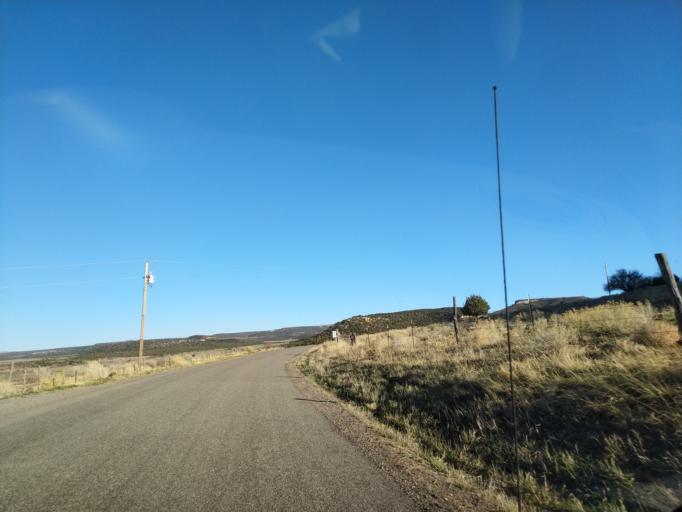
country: US
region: Colorado
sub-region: Mesa County
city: Loma
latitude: 38.9509
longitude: -108.9881
